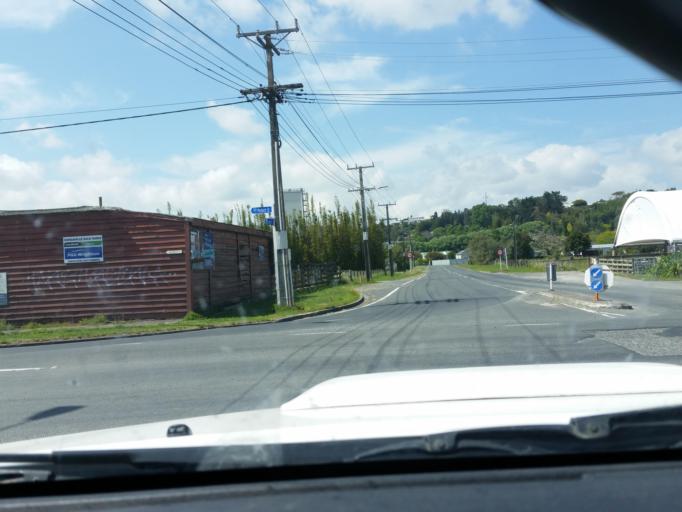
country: NZ
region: Northland
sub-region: Kaipara District
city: Dargaville
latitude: -35.9510
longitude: 173.8629
